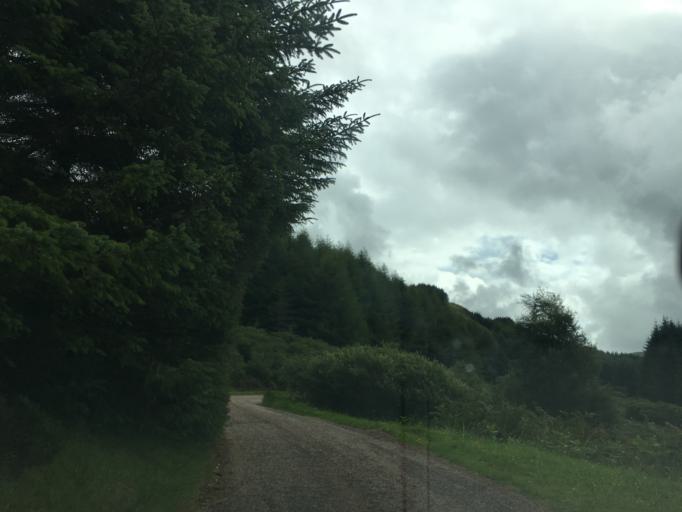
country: GB
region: Scotland
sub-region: Argyll and Bute
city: Oban
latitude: 56.2522
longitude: -5.4377
